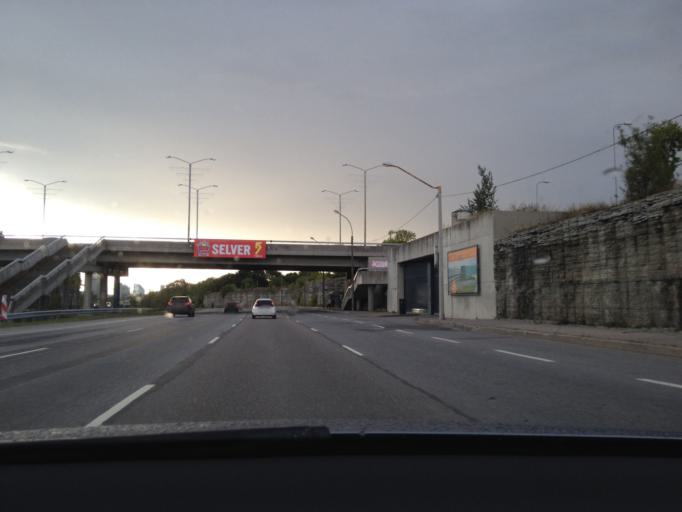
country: EE
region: Harju
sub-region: Tallinna linn
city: Tallinn
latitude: 59.4351
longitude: 24.8001
